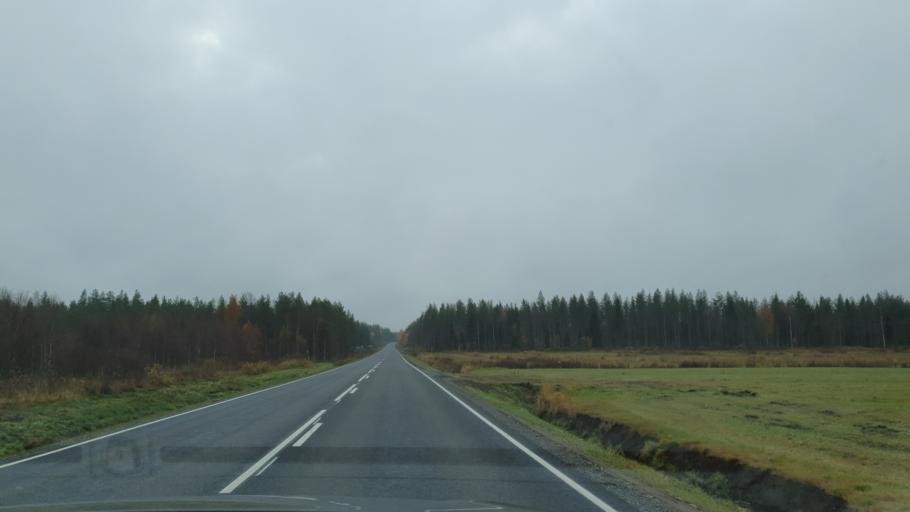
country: FI
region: Lapland
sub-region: Rovaniemi
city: Ranua
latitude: 66.0798
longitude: 26.3607
